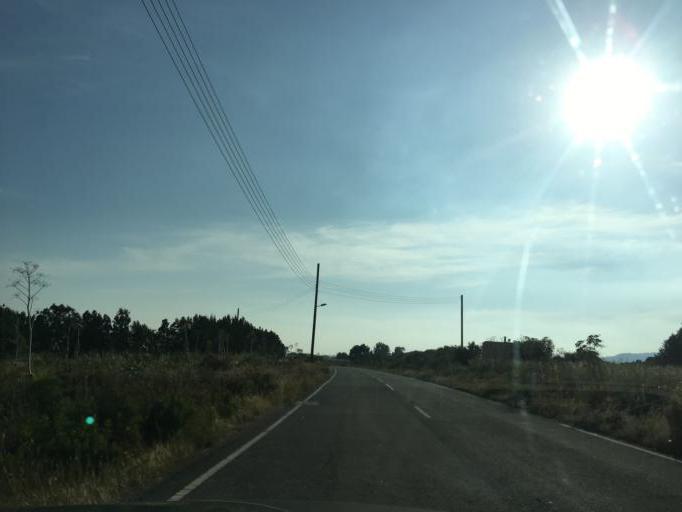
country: CY
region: Larnaka
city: Kofinou
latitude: 34.7722
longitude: 33.4496
